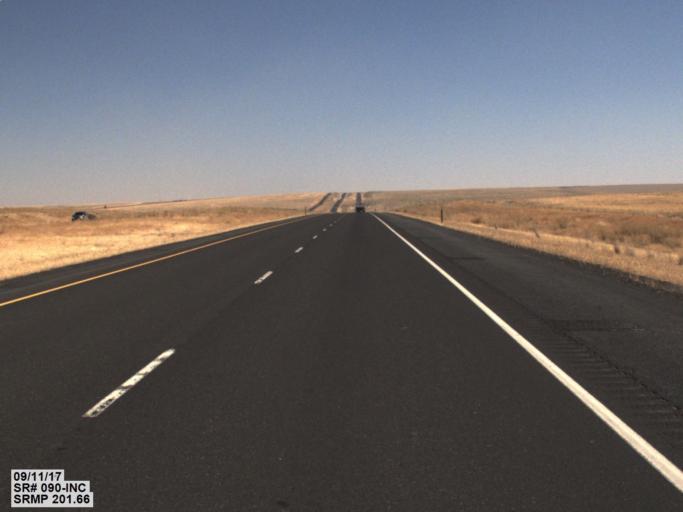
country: US
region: Washington
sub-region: Grant County
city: Warden
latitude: 47.0860
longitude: -118.7746
